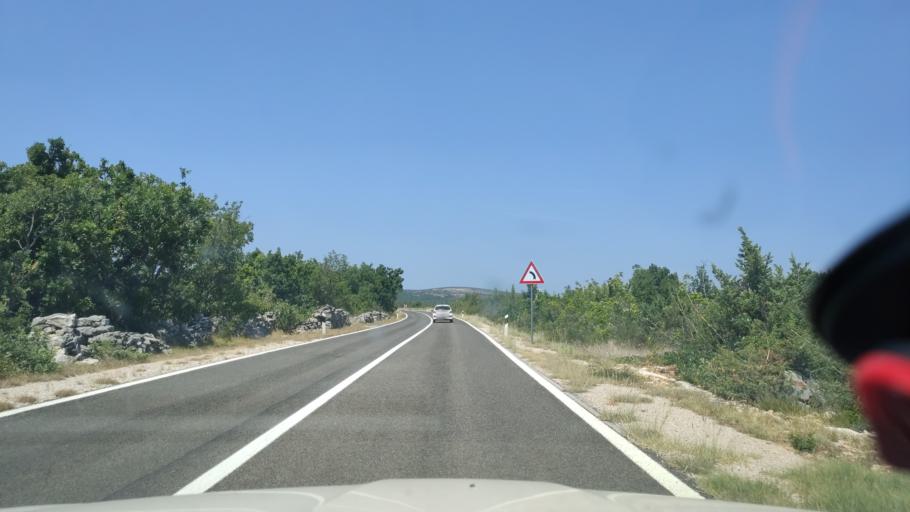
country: HR
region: Sibensko-Kniniska
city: Kistanje
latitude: 43.9714
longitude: 15.9007
